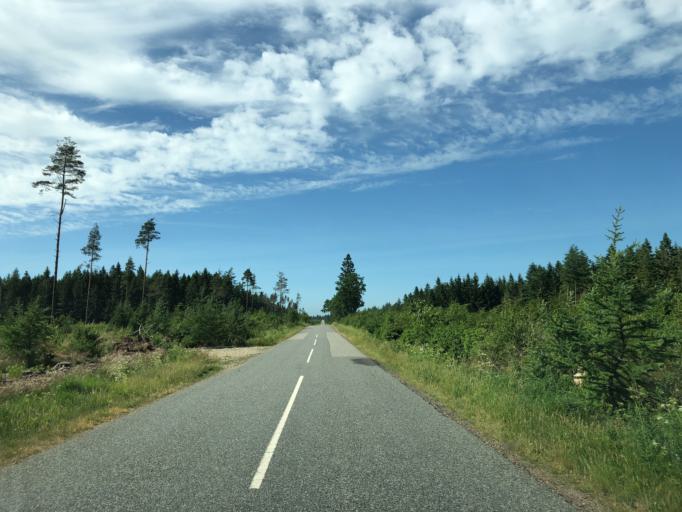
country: DK
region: Central Jutland
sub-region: Herning Kommune
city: Kibaek
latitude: 56.0497
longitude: 8.9281
